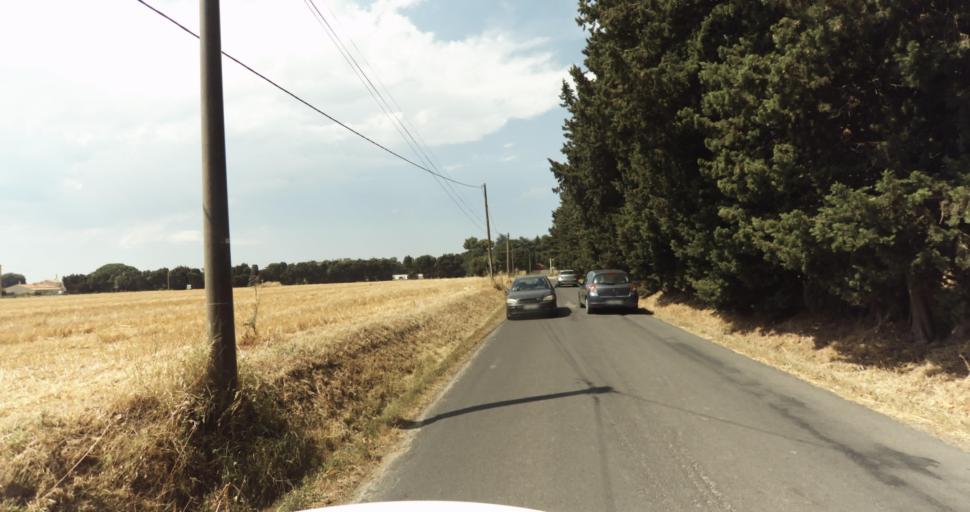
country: FR
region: Languedoc-Roussillon
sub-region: Departement des Pyrenees-Orientales
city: Latour-Bas-Elne
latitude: 42.6012
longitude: 3.0071
